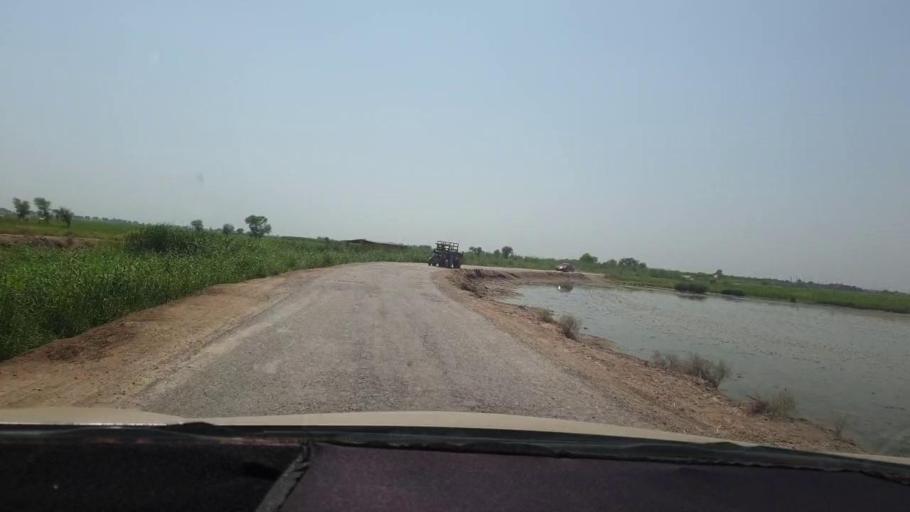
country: PK
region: Sindh
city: Shahdadkot
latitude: 27.8424
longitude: 67.9477
